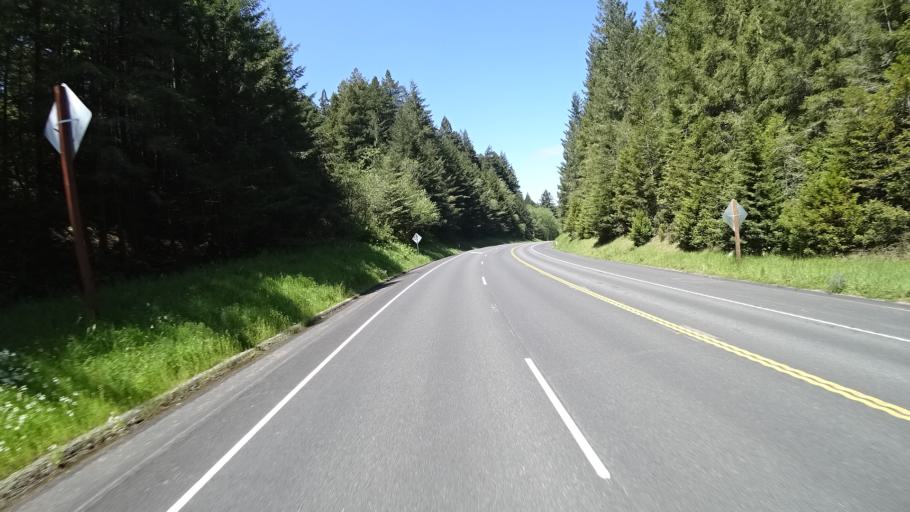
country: US
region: California
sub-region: Humboldt County
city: Blue Lake
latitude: 40.8843
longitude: -123.9691
